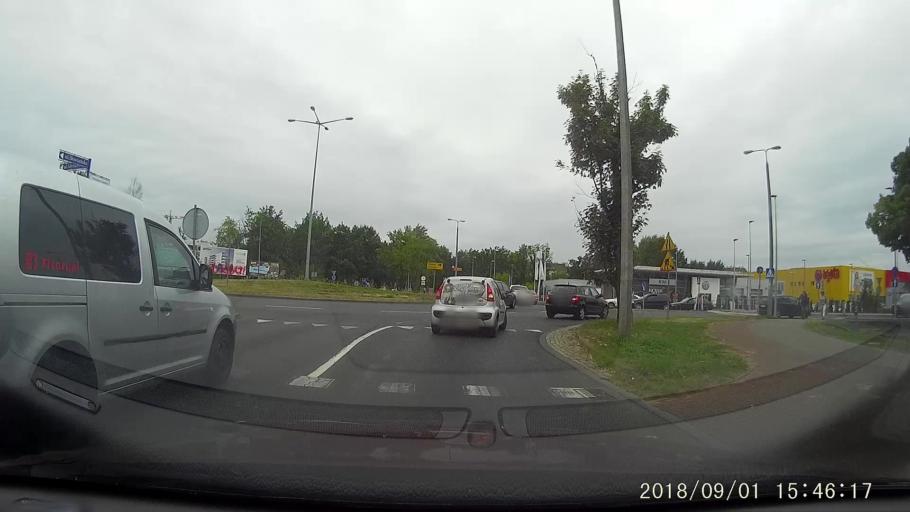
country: PL
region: Lubusz
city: Gorzow Wielkopolski
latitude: 52.7373
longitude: 15.2007
